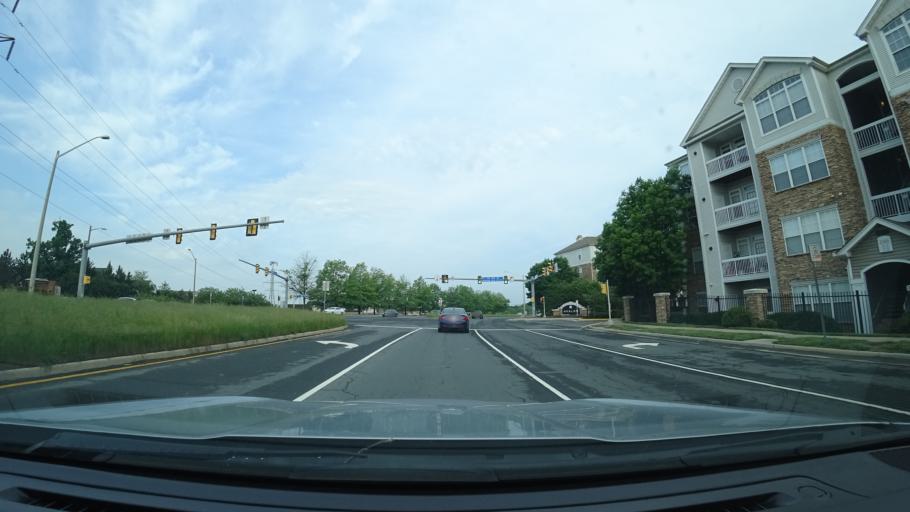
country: US
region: Virginia
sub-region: Fairfax County
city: Floris
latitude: 38.9511
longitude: -77.4051
